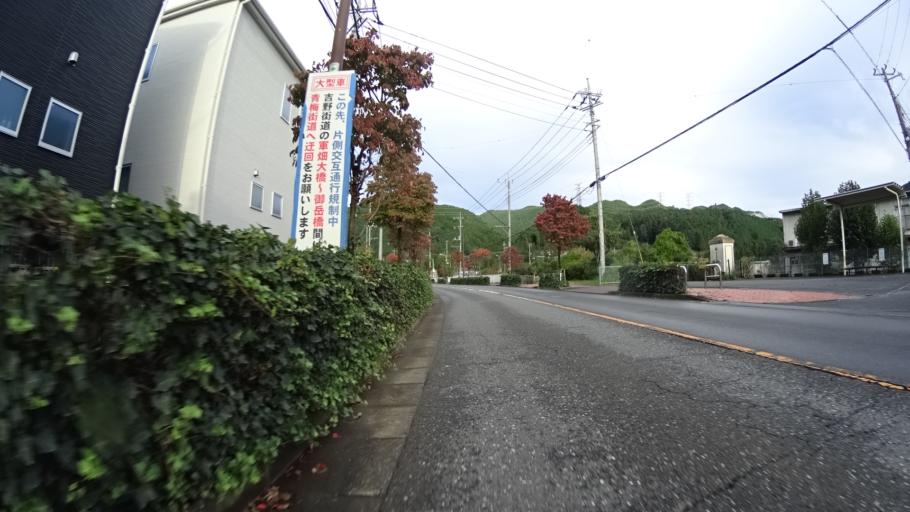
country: JP
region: Tokyo
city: Ome
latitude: 35.8024
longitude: 139.2093
